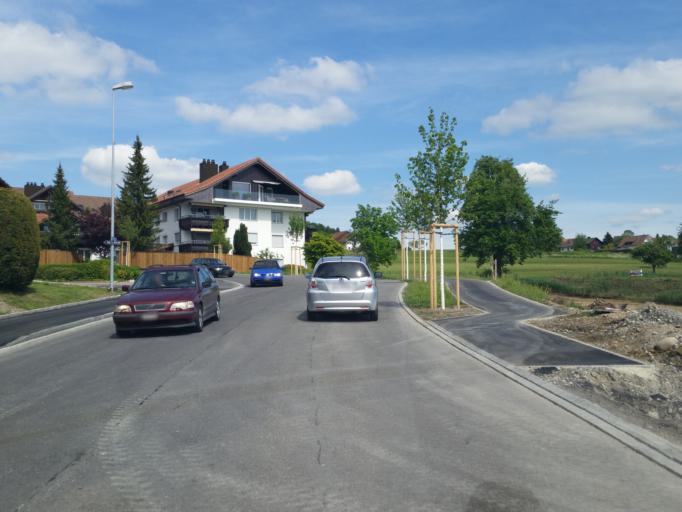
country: CH
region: Aargau
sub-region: Bezirk Bremgarten
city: Unterlunkhofen
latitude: 47.3342
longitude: 8.3862
